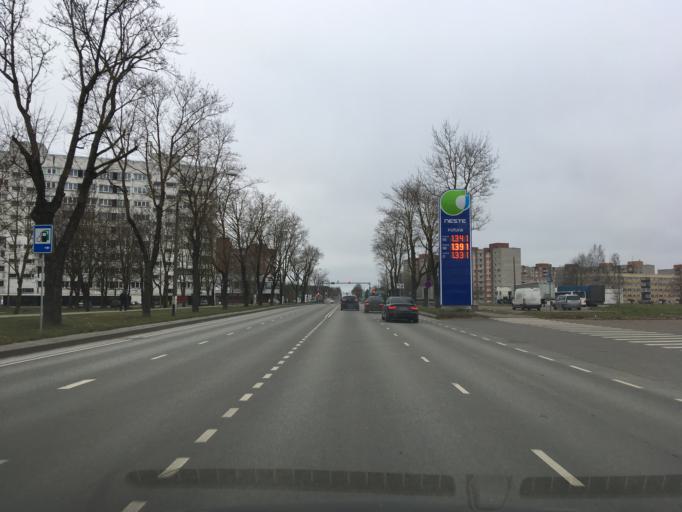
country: EE
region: Ida-Virumaa
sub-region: Narva linn
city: Narva
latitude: 59.3820
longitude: 28.1689
